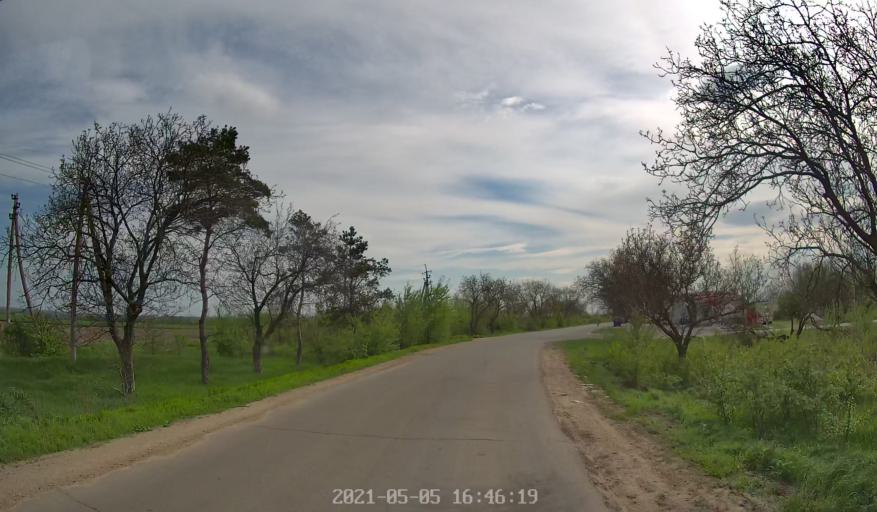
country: MD
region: Criuleni
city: Criuleni
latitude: 47.1013
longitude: 29.1918
